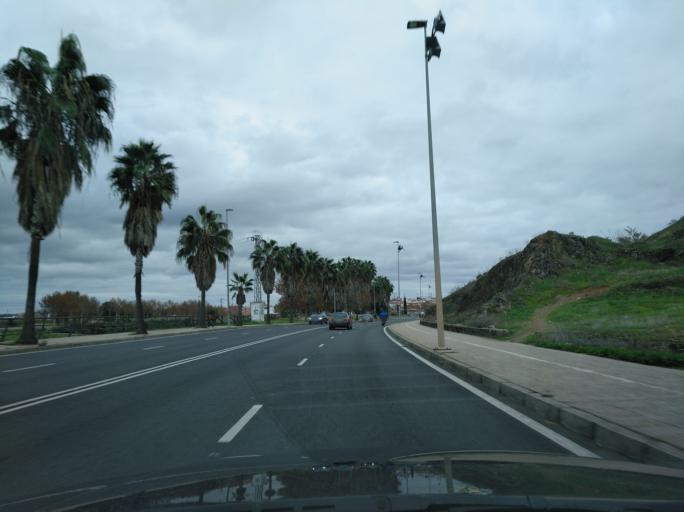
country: ES
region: Extremadura
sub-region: Provincia de Badajoz
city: Badajoz
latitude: 38.8843
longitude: -6.9669
